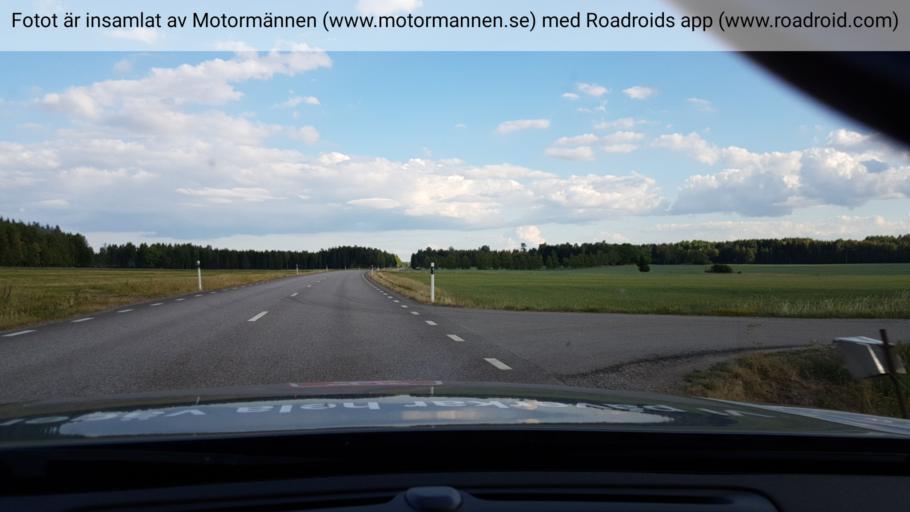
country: SE
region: Uppsala
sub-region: Heby Kommun
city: Morgongava
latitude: 59.8788
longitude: 16.9210
